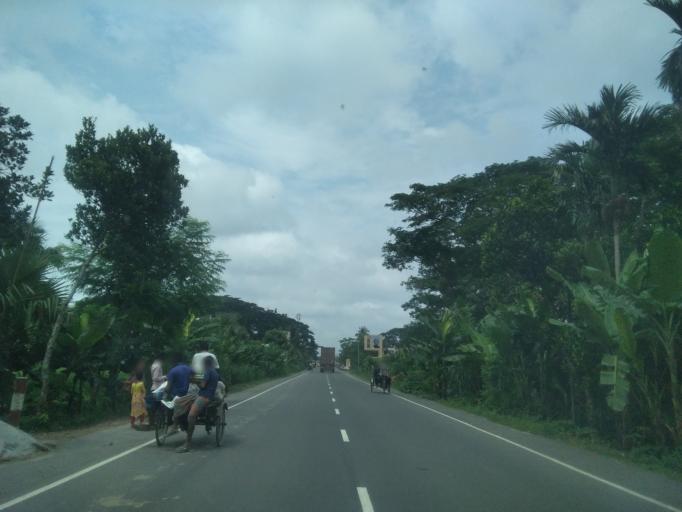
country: BD
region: Khulna
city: Kesabpur
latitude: 22.8142
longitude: 89.2473
